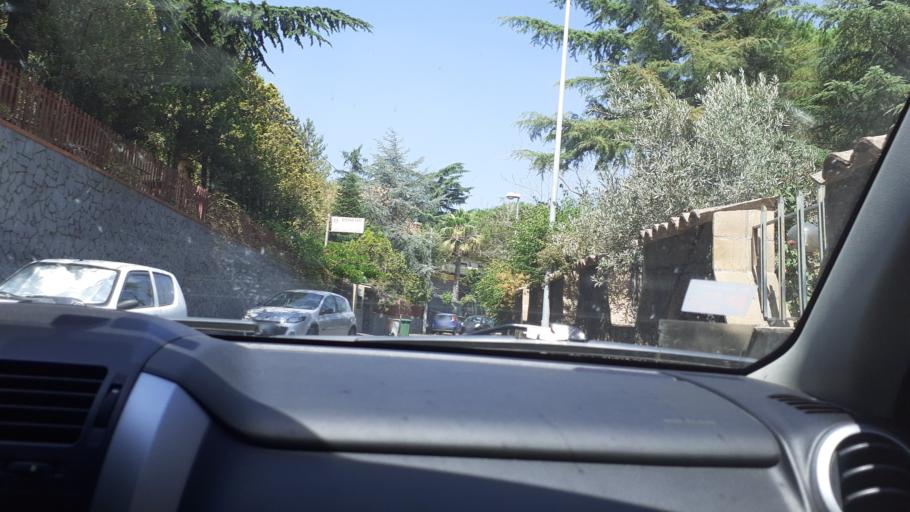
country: IT
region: Sicily
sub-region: Catania
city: Nicolosi
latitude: 37.6195
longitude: 15.0308
